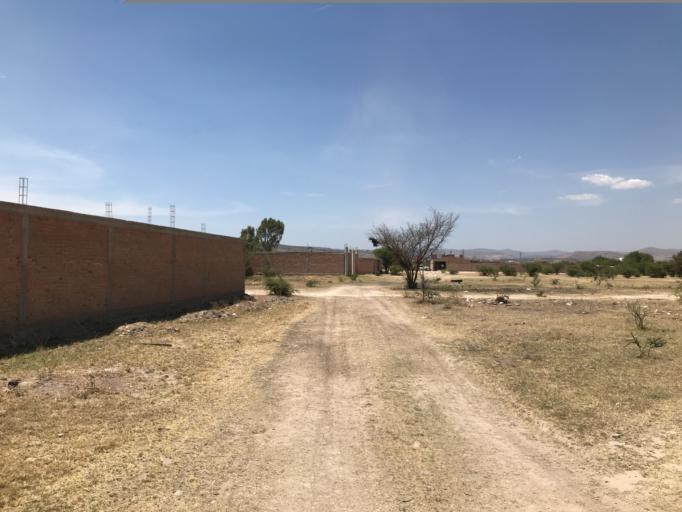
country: MX
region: Durango
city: Victoria de Durango
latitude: 23.9795
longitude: -104.6848
